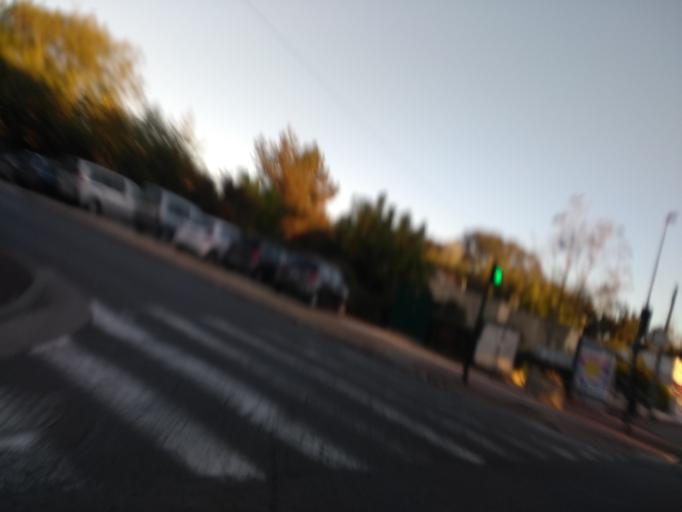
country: FR
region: Aquitaine
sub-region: Departement de la Gironde
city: Gradignan
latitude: 44.7839
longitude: -0.6067
